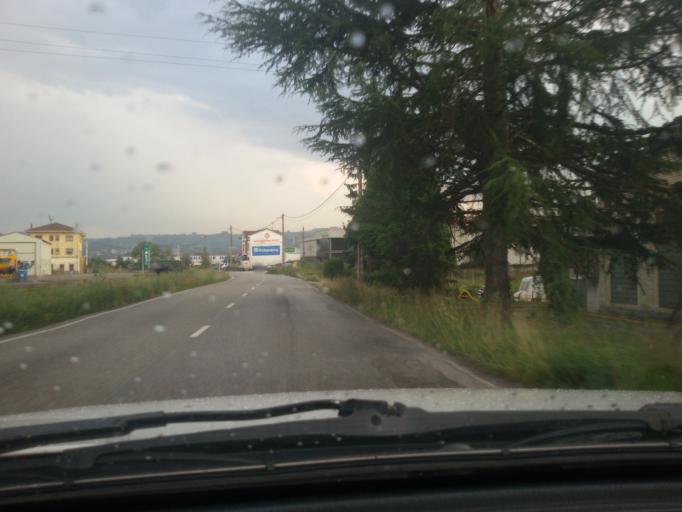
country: ES
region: Asturias
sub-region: Province of Asturias
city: Lugones
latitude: 43.3905
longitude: -5.7871
